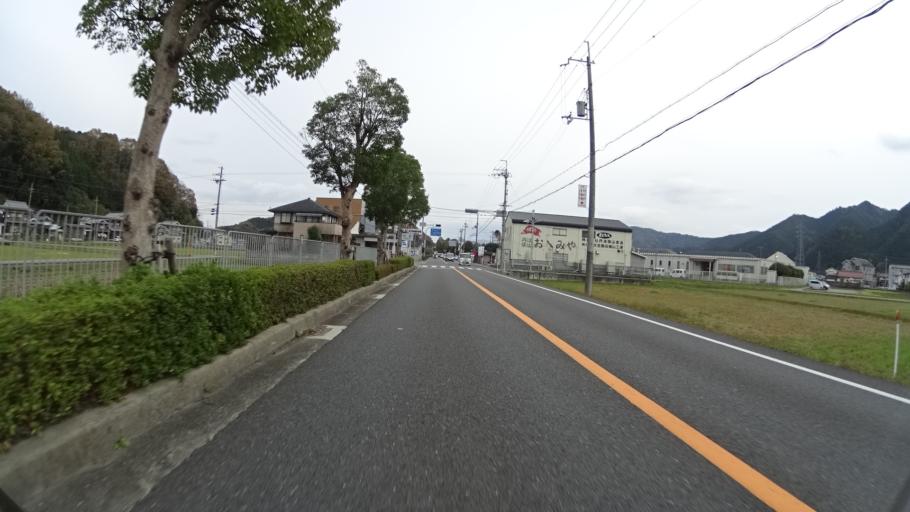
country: JP
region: Hyogo
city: Sasayama
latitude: 35.0644
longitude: 135.1876
